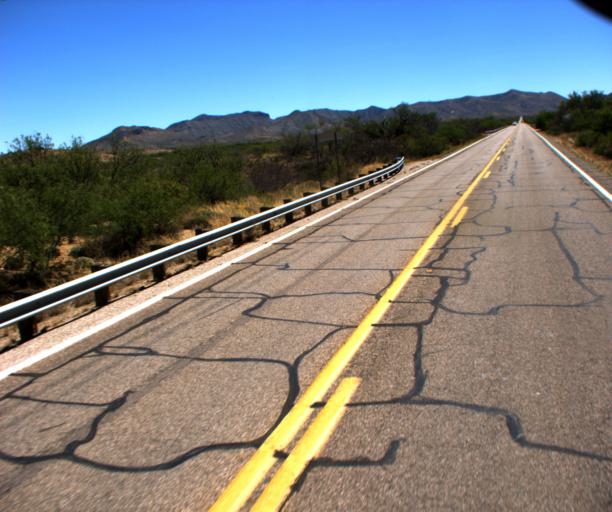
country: US
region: Arizona
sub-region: Pima County
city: Vail
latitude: 31.9627
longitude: -110.6718
